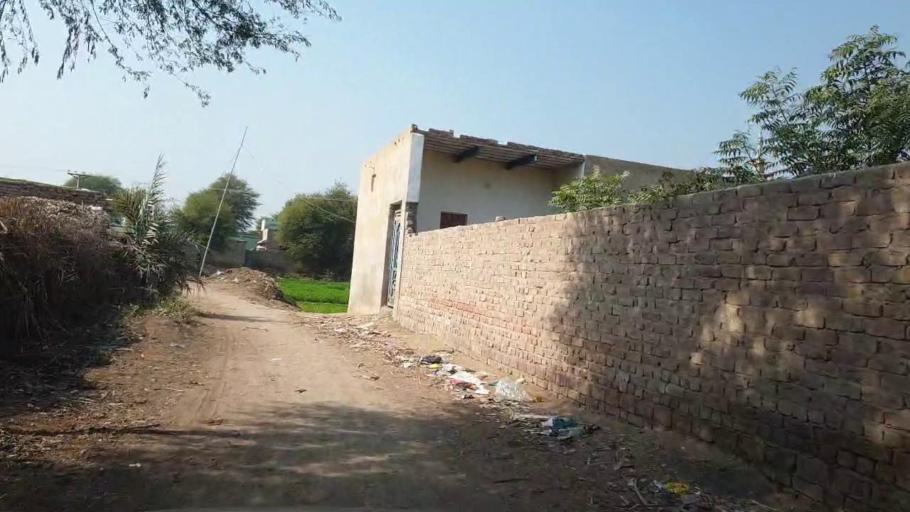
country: PK
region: Sindh
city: Bhit Shah
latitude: 25.7270
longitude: 68.5409
